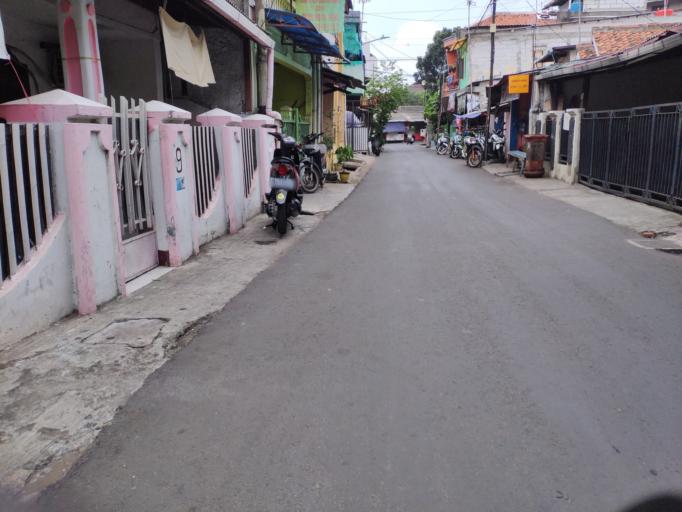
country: ID
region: Jakarta Raya
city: Jakarta
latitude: -6.2106
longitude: 106.8635
